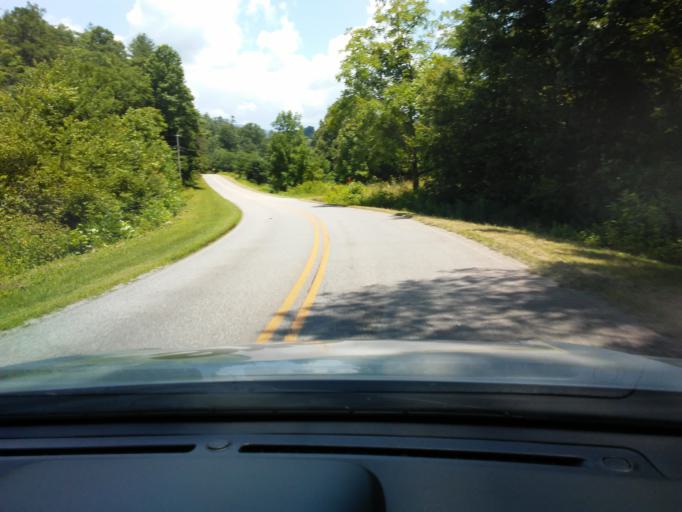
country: US
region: Georgia
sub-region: Towns County
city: Hiawassee
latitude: 34.8672
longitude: -83.7438
